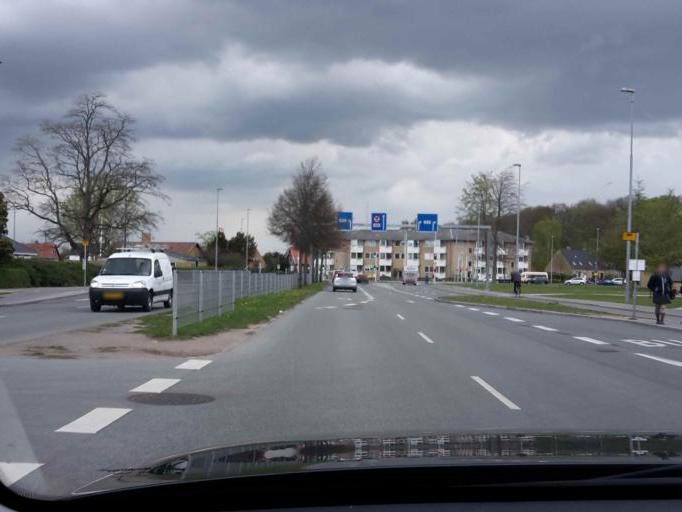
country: DK
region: South Denmark
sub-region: Odense Kommune
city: Odense
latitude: 55.3805
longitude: 10.4081
